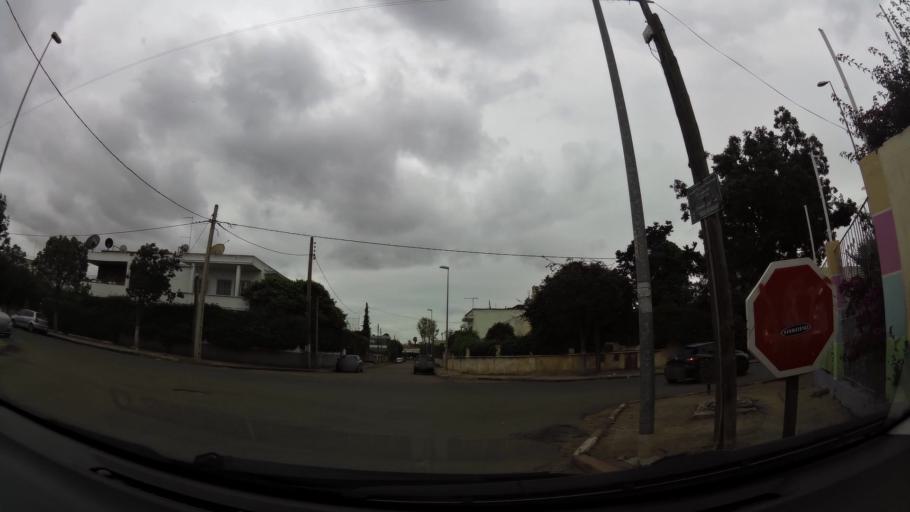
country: MA
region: Grand Casablanca
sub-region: Casablanca
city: Casablanca
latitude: 33.5922
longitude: -7.6474
